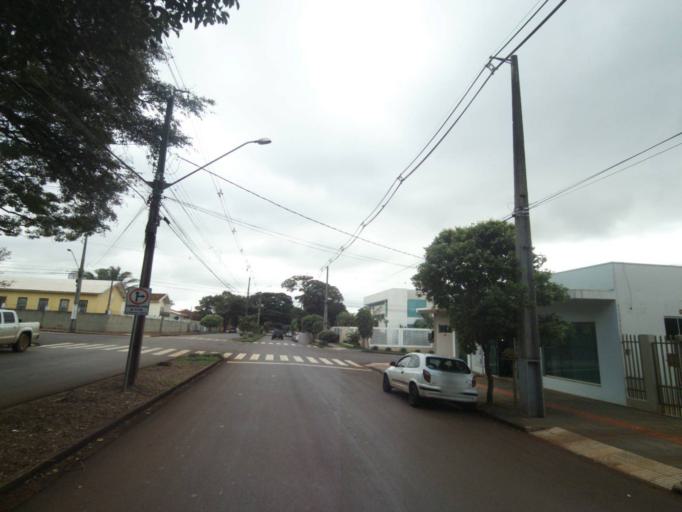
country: BR
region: Parana
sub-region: Campo Mourao
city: Campo Mourao
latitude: -24.0462
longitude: -52.3731
